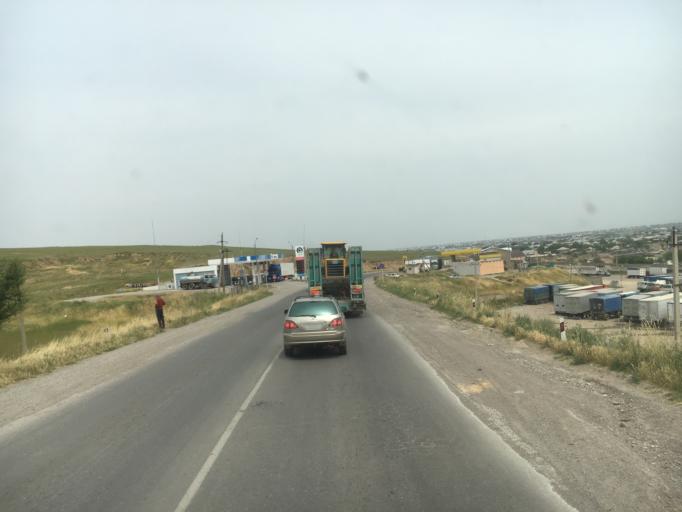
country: KZ
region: Ongtustik Qazaqstan
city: Shymkent
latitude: 42.3263
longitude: 69.5140
